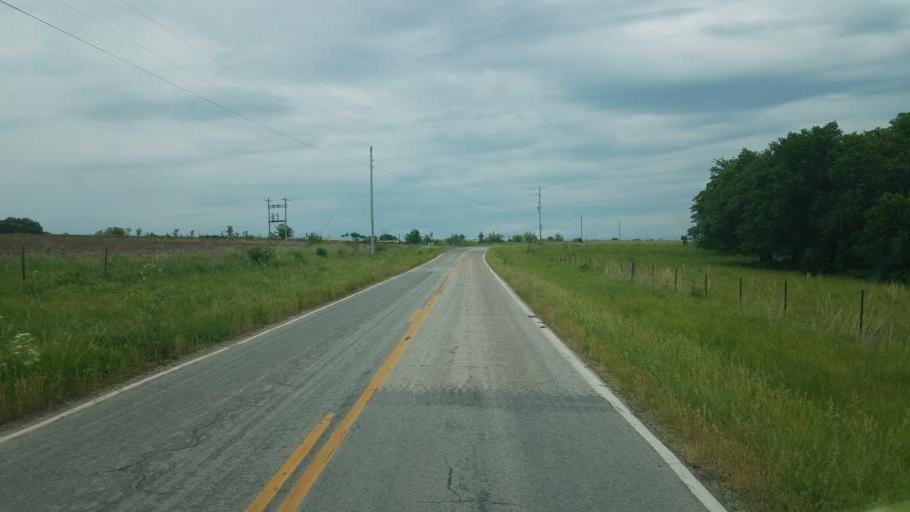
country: US
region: Missouri
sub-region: Moniteau County
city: California
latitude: 38.6706
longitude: -92.5860
